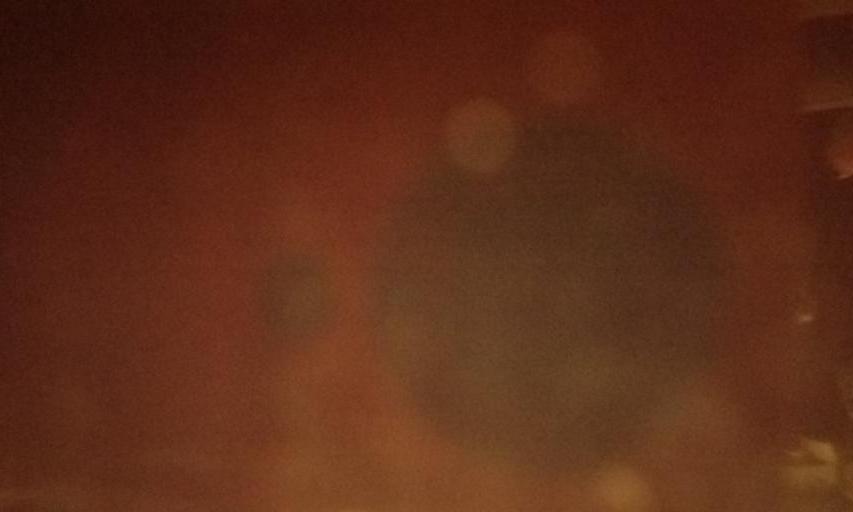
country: JP
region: Hyogo
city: Kobe
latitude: 34.6858
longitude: 135.1018
